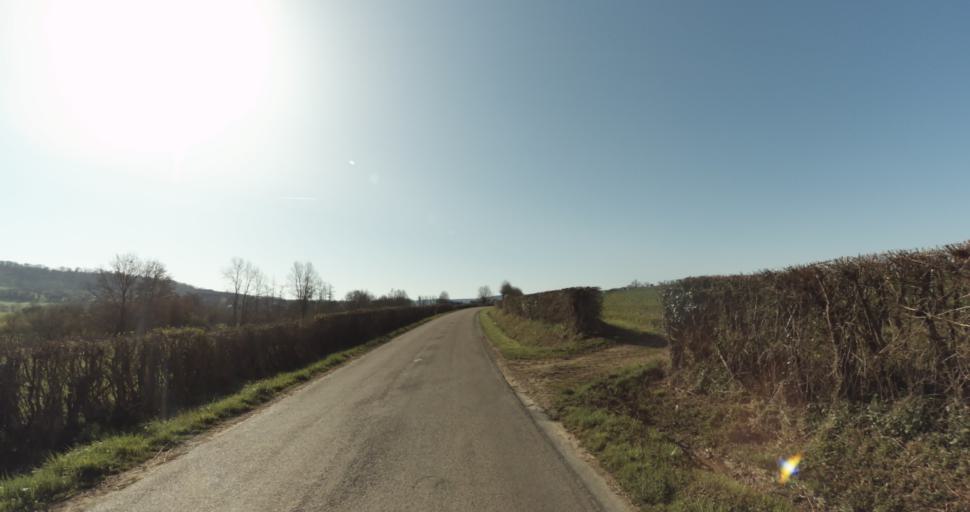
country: FR
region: Lower Normandy
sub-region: Departement du Calvados
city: Saint-Pierre-sur-Dives
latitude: 48.9854
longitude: 0.0314
